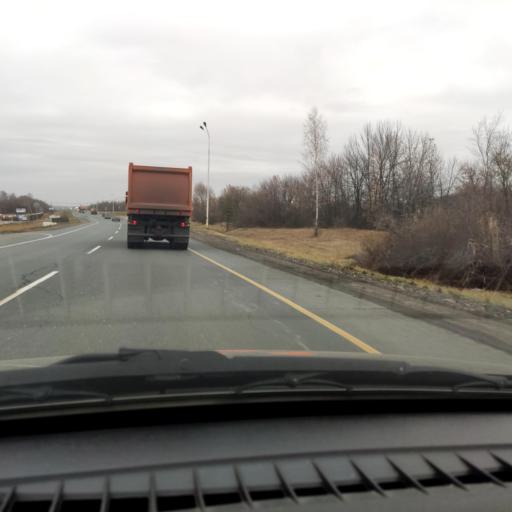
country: RU
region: Samara
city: Zhigulevsk
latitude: 53.3430
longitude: 49.4481
